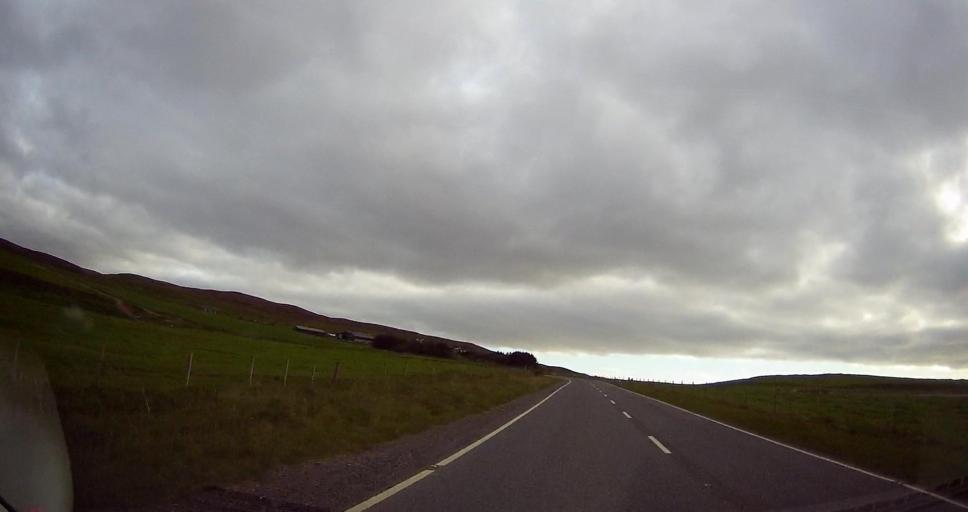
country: GB
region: Scotland
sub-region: Shetland Islands
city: Lerwick
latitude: 60.4337
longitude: -1.2912
